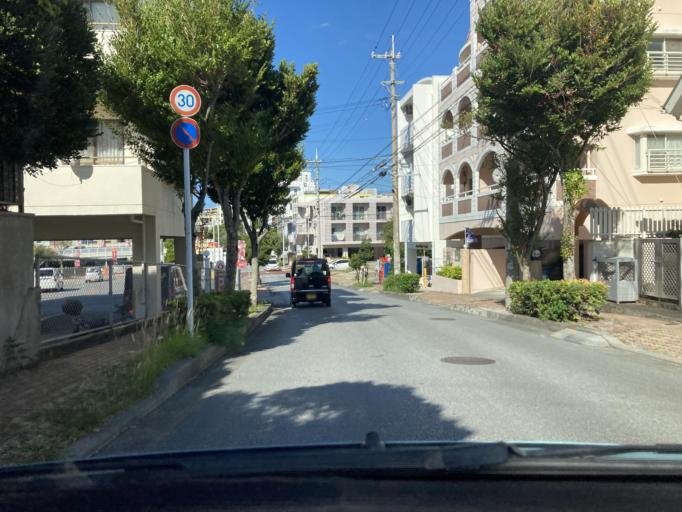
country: JP
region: Okinawa
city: Tomigusuku
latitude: 26.1880
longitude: 127.6589
